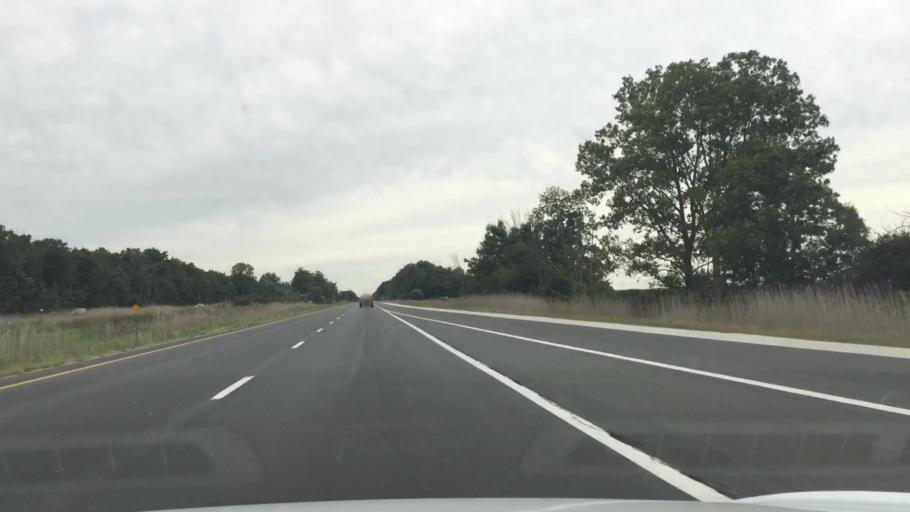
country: CA
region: Ontario
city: Camlachie
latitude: 42.9916
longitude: -82.0094
